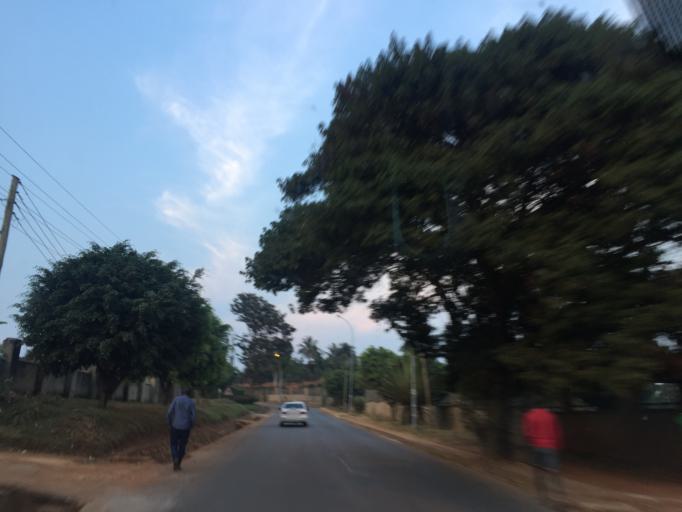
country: UG
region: Central Region
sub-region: Kampala District
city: Kampala
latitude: 0.2421
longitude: 32.6269
